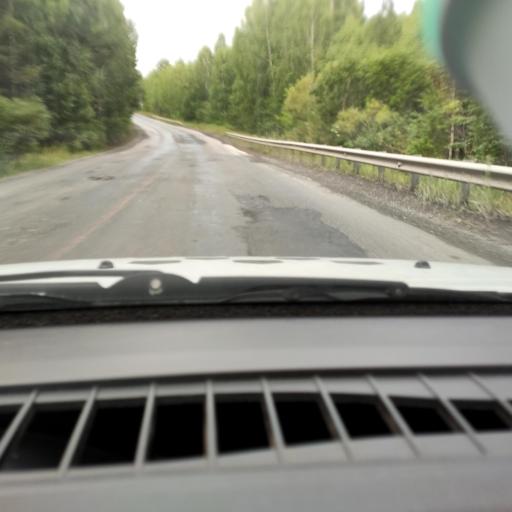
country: RU
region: Chelyabinsk
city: Karabash
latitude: 55.5219
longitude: 60.3335
